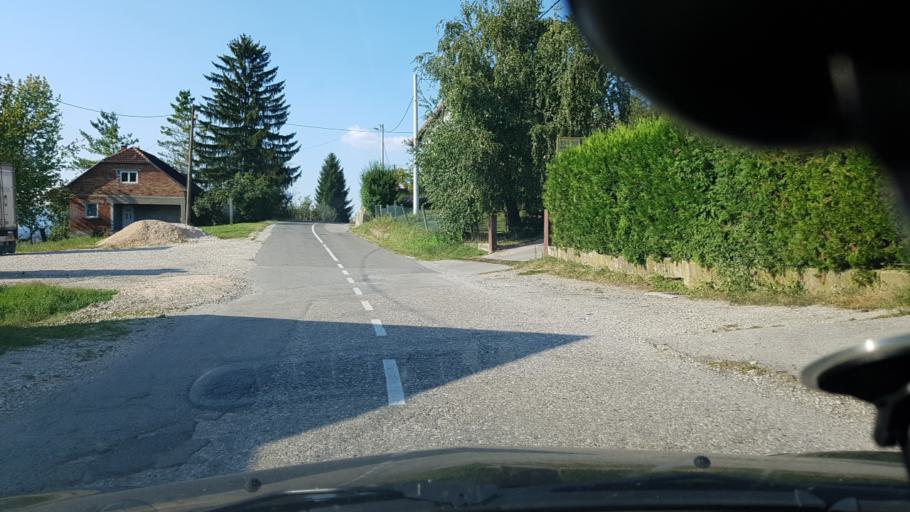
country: HR
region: Zagrebacka
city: Pojatno
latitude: 45.9244
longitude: 15.7176
